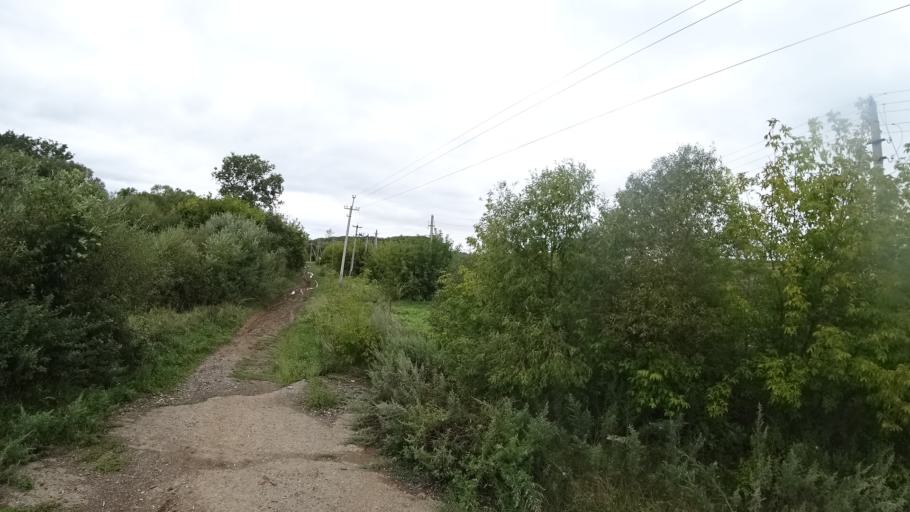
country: RU
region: Primorskiy
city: Chernigovka
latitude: 44.4545
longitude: 132.5902
